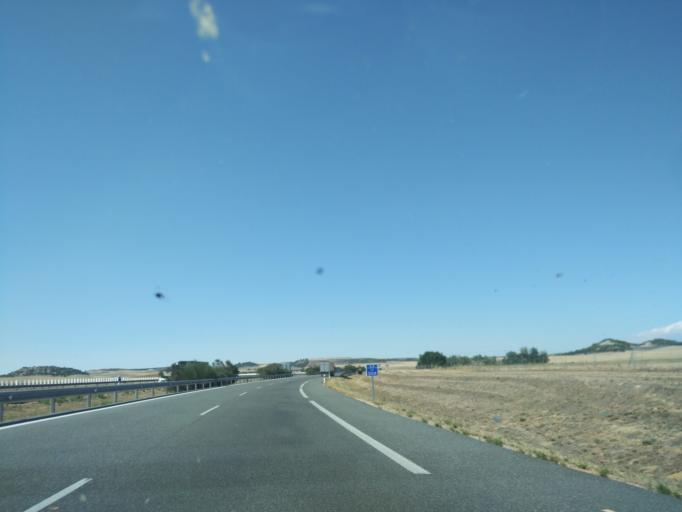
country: ES
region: Castille and Leon
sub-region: Provincia de Valladolid
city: Mota del Marques
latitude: 41.6347
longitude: -5.1875
